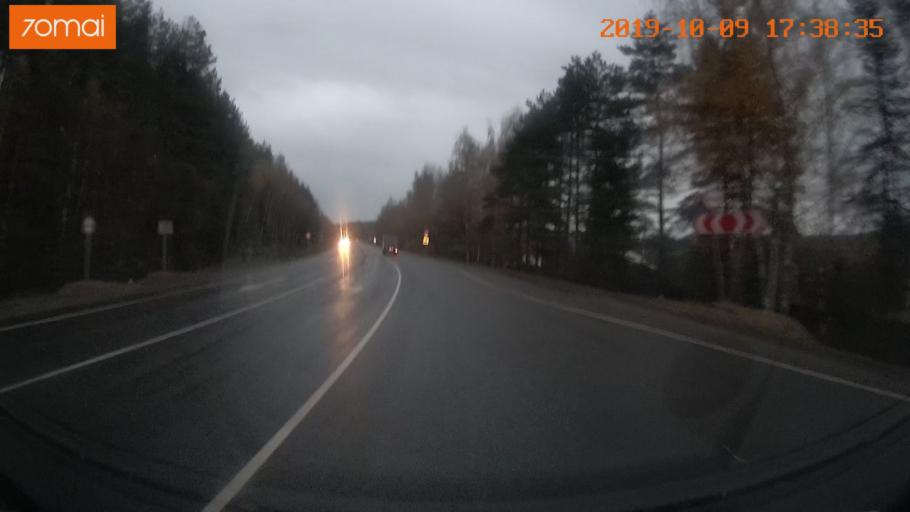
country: RU
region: Ivanovo
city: Bogorodskoye
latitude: 57.0697
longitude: 40.9515
